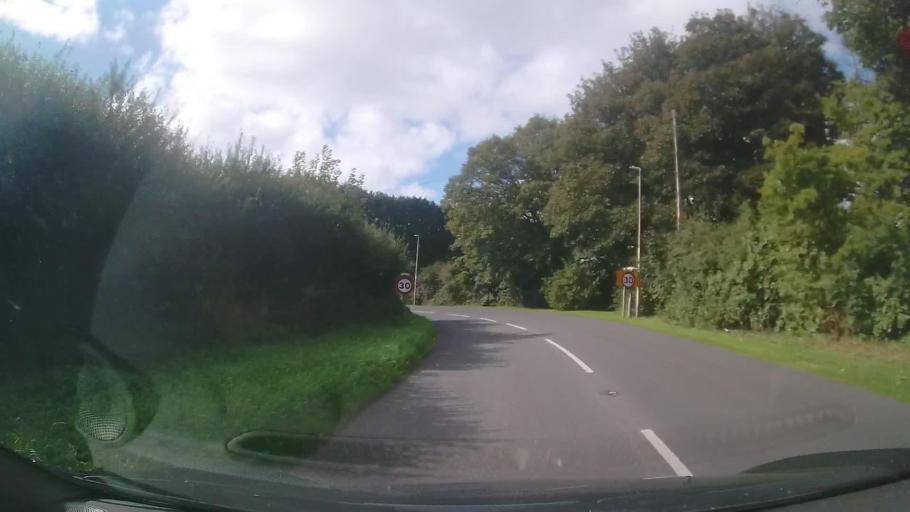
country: GB
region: Wales
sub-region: Pembrokeshire
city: Manorbier
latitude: 51.6528
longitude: -4.7662
